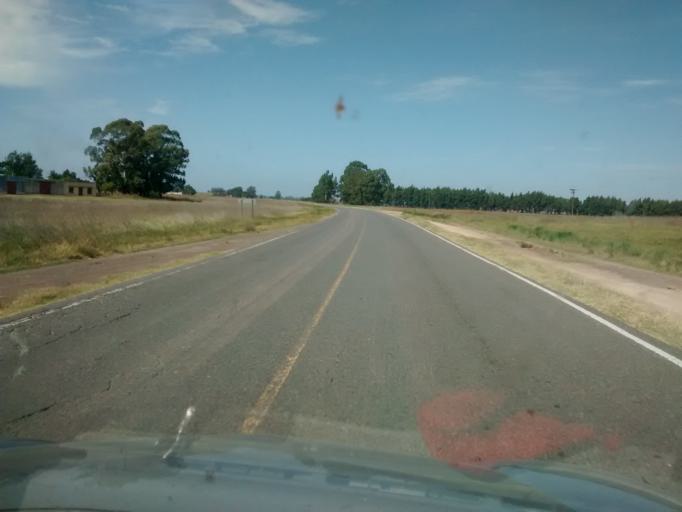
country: AR
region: Buenos Aires
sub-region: Partido de Balcarce
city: Balcarce
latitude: -37.6445
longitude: -58.4881
